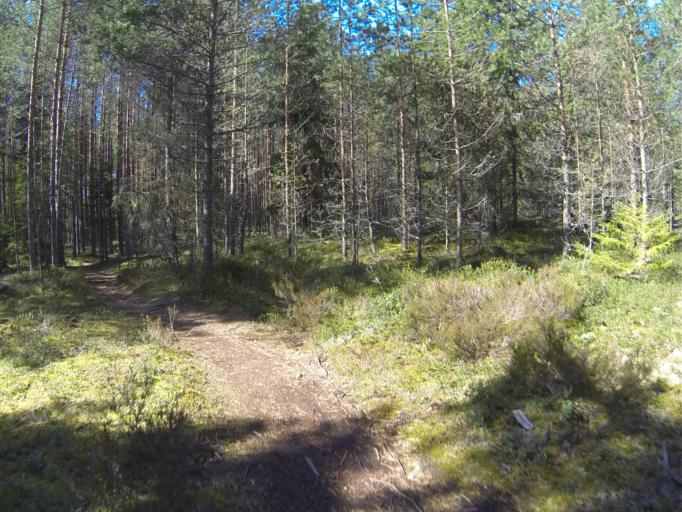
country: FI
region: Varsinais-Suomi
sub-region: Salo
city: Salo
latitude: 60.3947
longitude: 23.2051
